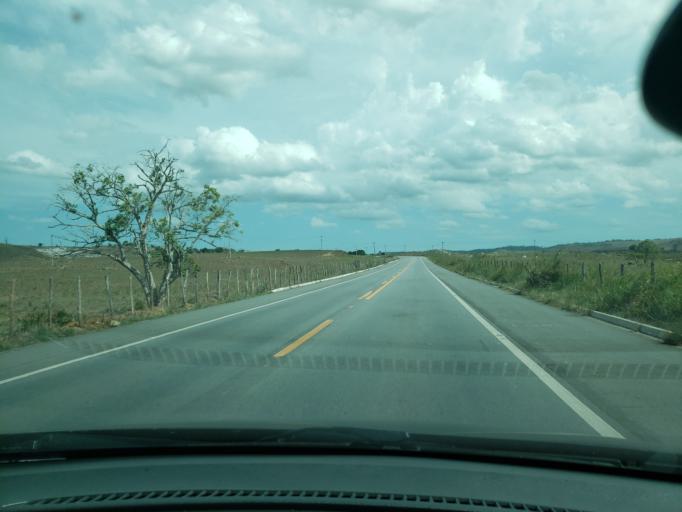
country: BR
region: Alagoas
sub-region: Murici
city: Murici
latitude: -9.2948
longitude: -35.9589
